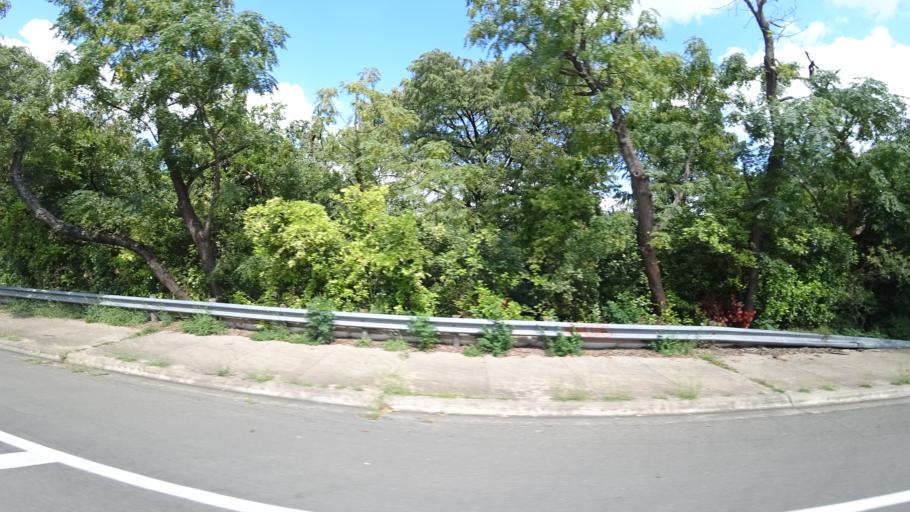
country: US
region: Texas
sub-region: Travis County
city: West Lake Hills
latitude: 30.3625
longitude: -97.7477
